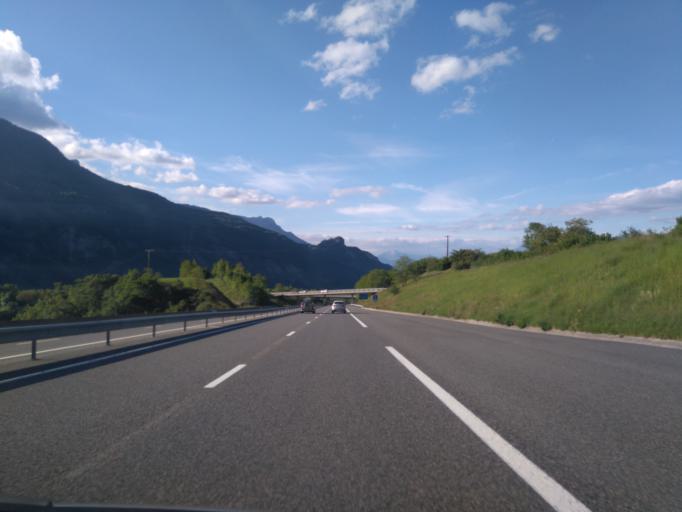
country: FR
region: Rhone-Alpes
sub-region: Departement de l'Isere
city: Vif
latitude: 45.0299
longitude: 5.6626
